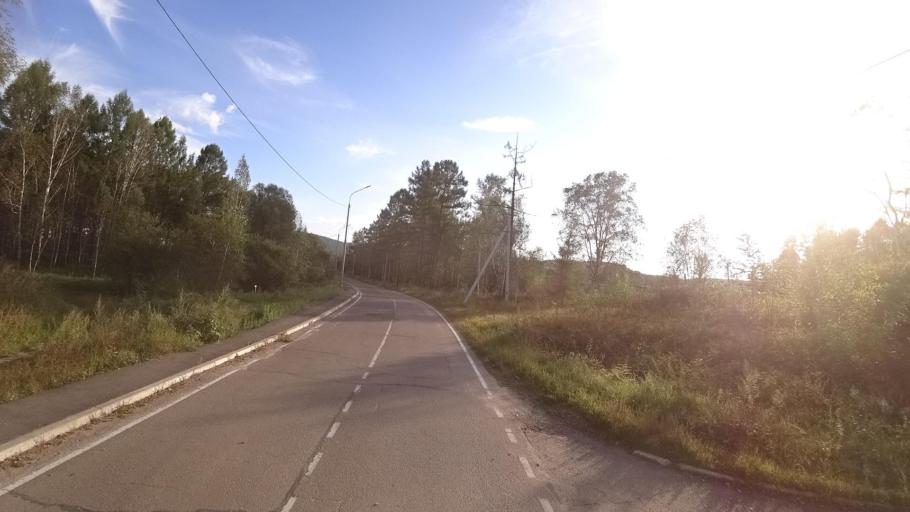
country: RU
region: Jewish Autonomous Oblast
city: Kul'dur
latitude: 49.2055
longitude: 131.6208
